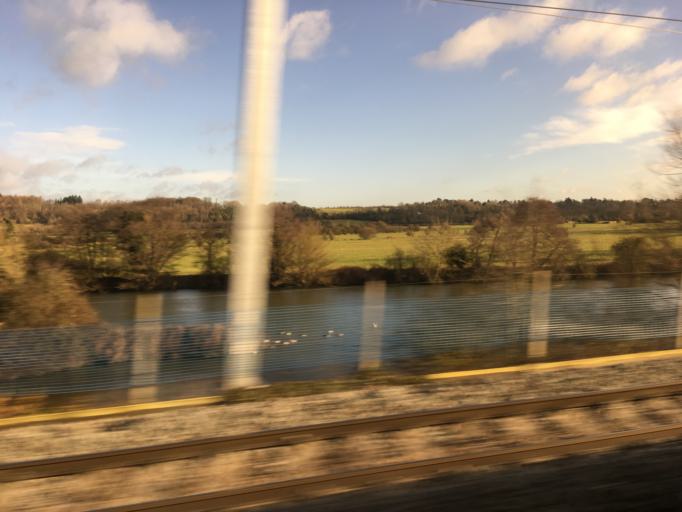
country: GB
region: England
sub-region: West Berkshire
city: Tilehurst
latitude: 51.4673
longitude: -1.0207
